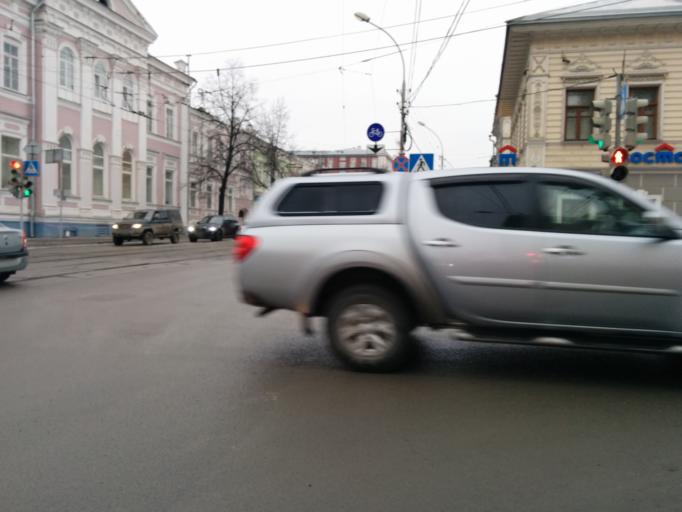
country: RU
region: Perm
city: Perm
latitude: 58.0125
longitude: 56.2431
